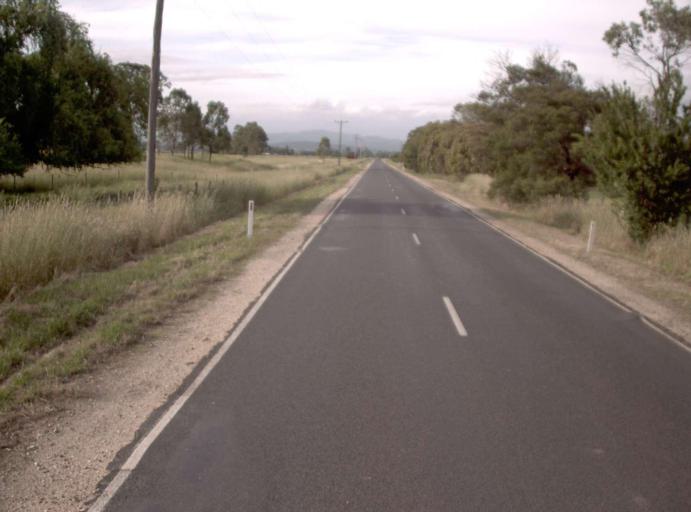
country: AU
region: Victoria
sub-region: Wellington
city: Sale
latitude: -37.9075
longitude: 146.9951
